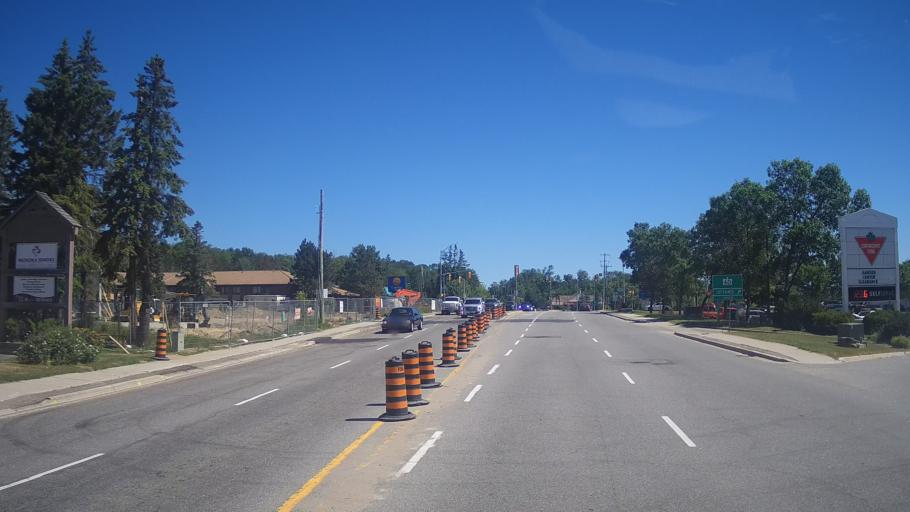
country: CA
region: Ontario
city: Huntsville
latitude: 45.3344
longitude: -79.2055
